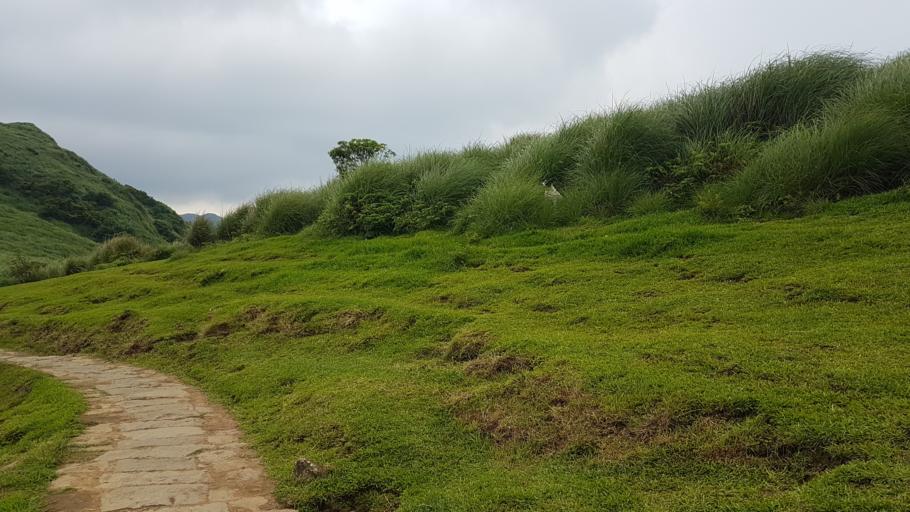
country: TW
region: Taipei
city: Taipei
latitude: 25.1668
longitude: 121.5762
